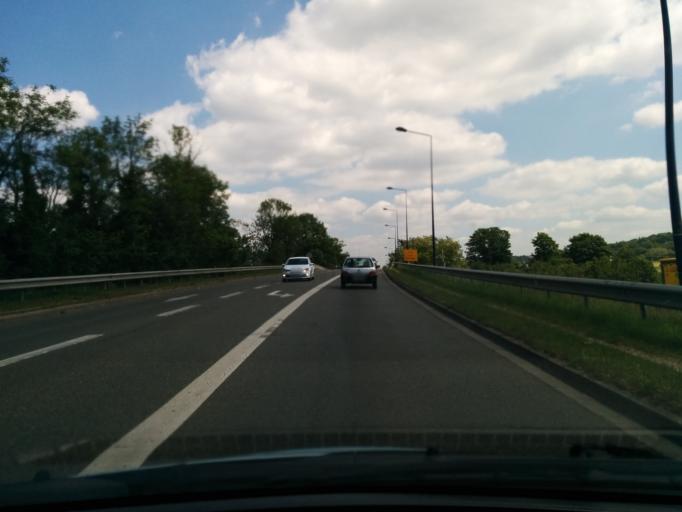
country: FR
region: Ile-de-France
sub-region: Departement des Yvelines
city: Epone
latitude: 48.9578
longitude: 1.8303
